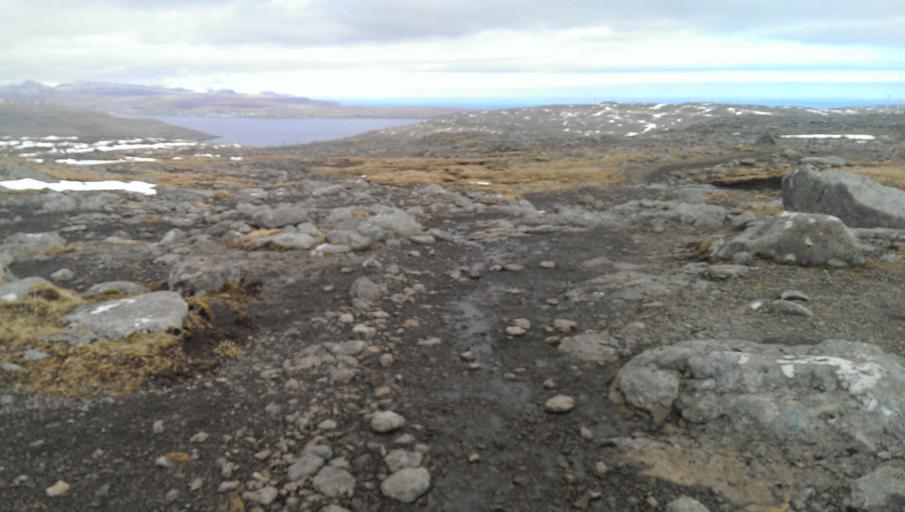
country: FO
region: Streymoy
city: Kollafjordhur
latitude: 62.0308
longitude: -6.8797
